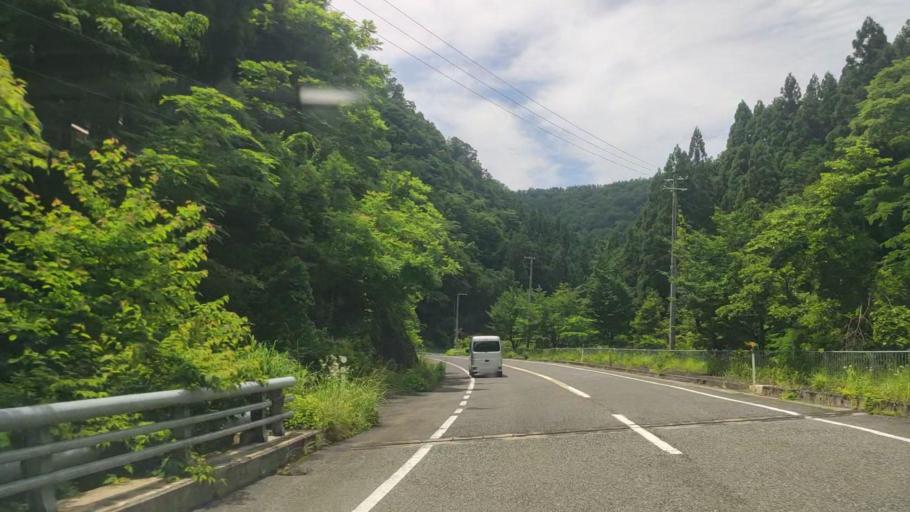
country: JP
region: Hyogo
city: Toyooka
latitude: 35.4843
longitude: 134.6144
